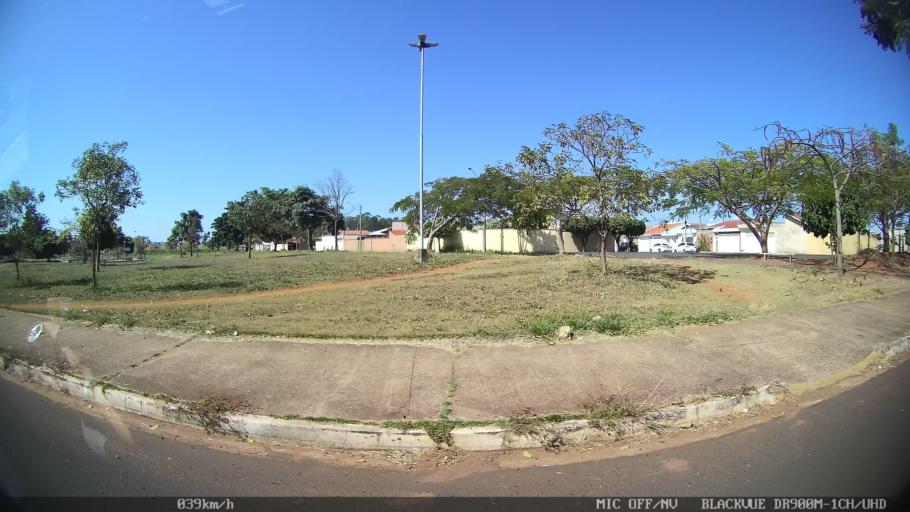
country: BR
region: Sao Paulo
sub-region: Batatais
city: Batatais
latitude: -20.8757
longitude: -47.5943
